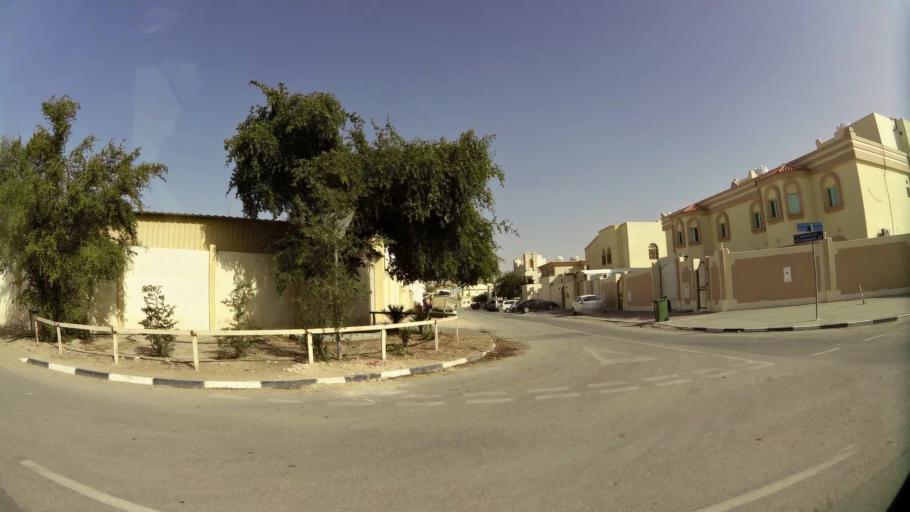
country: QA
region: Baladiyat ar Rayyan
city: Ar Rayyan
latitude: 25.3356
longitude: 51.4265
